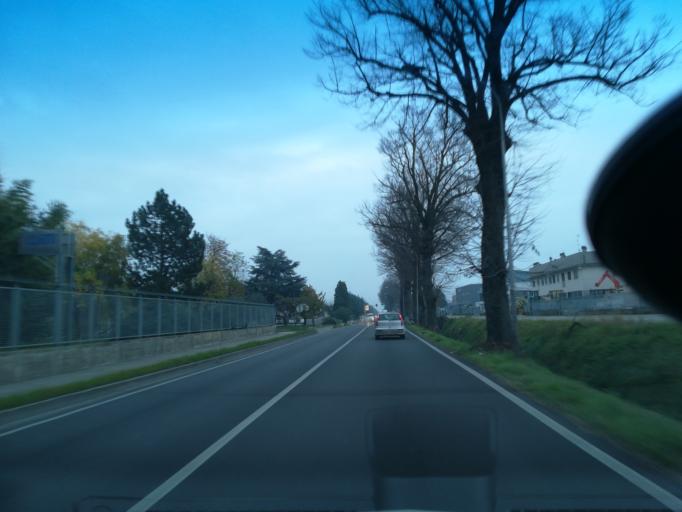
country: IT
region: Emilia-Romagna
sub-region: Provincia di Ravenna
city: Castel Bolognese
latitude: 44.3260
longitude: 11.7836
